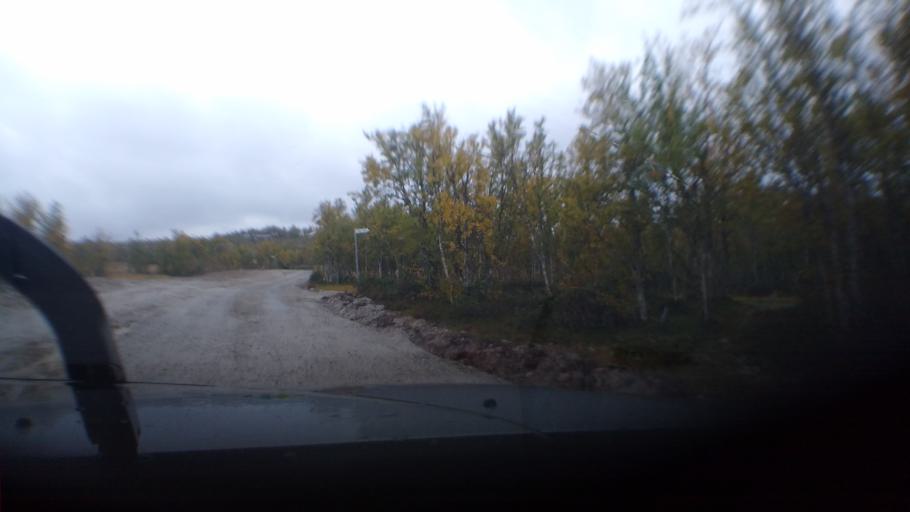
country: NO
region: Oppland
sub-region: Ringebu
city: Ringebu
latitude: 61.6553
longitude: 10.1029
